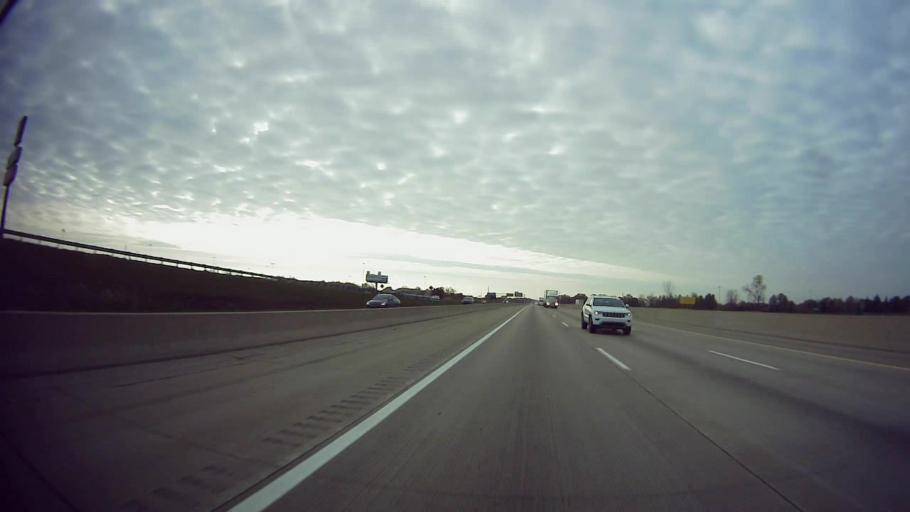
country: US
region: Michigan
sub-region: Wayne County
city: Woodhaven
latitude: 42.1378
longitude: -83.2414
